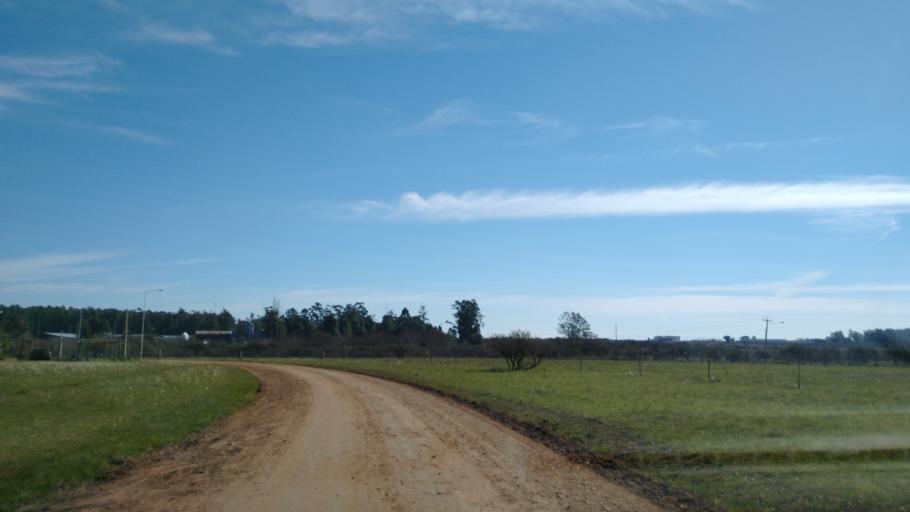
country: AR
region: Entre Rios
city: Chajari
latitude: -30.7419
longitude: -58.0105
